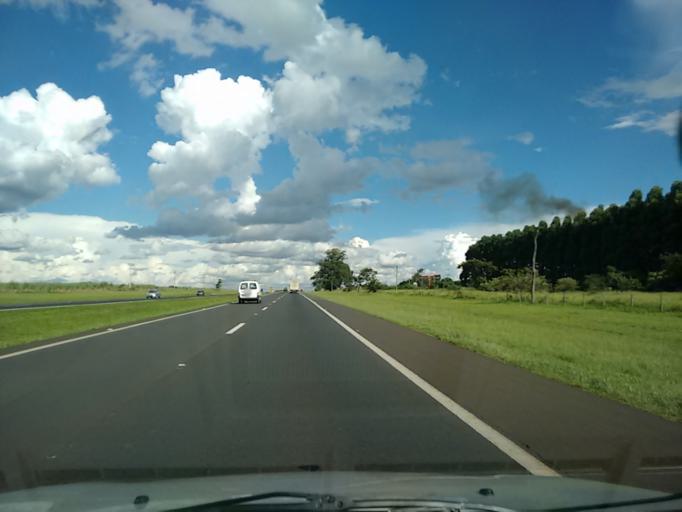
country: BR
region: Sao Paulo
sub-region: Ibate
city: Ibate
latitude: -21.9260
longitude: -48.0271
